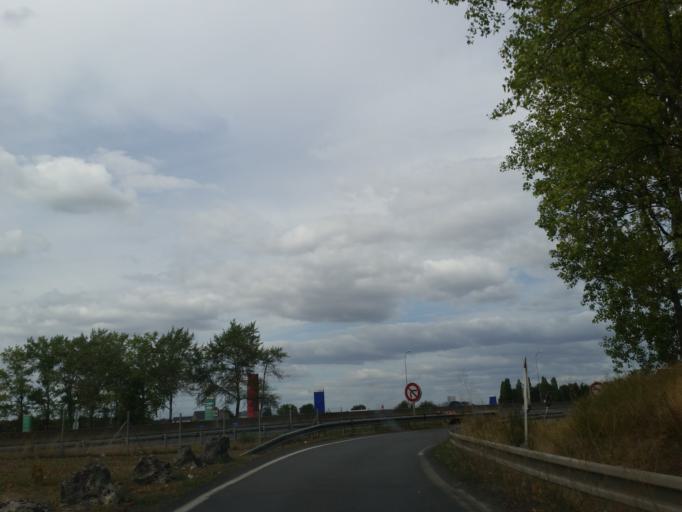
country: FR
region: Centre
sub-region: Departement d'Indre-et-Loire
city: Monnaie
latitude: 47.4748
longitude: 0.7777
